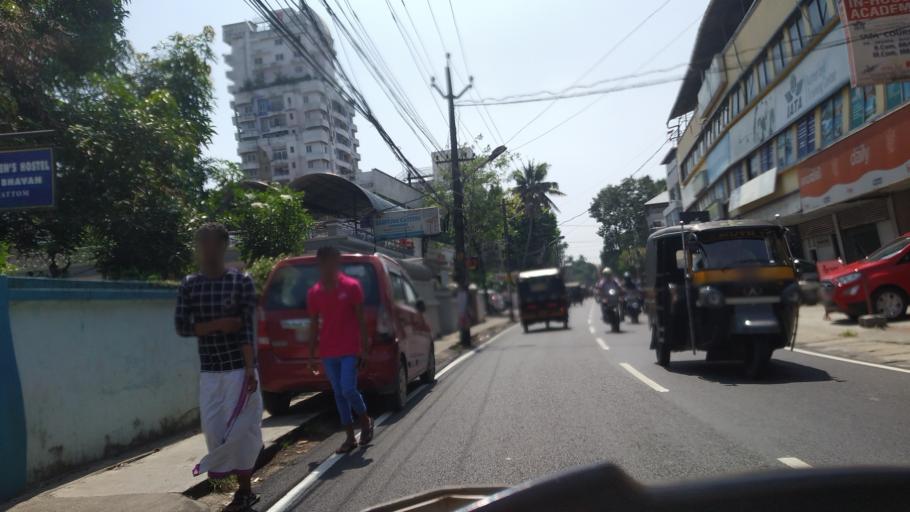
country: IN
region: Kerala
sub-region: Ernakulam
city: Elur
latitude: 9.9994
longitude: 76.3073
